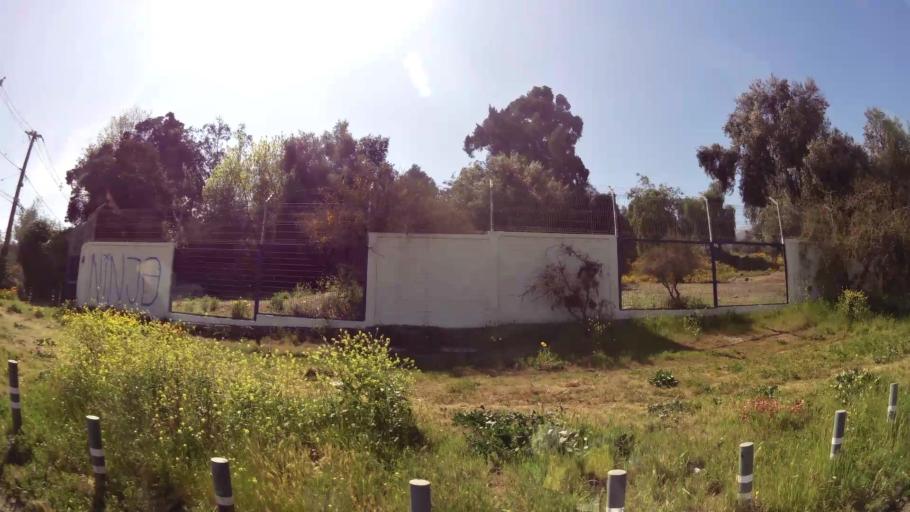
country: CL
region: Santiago Metropolitan
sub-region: Provincia de Santiago
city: Villa Presidente Frei, Nunoa, Santiago, Chile
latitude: -33.4367
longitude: -70.5186
